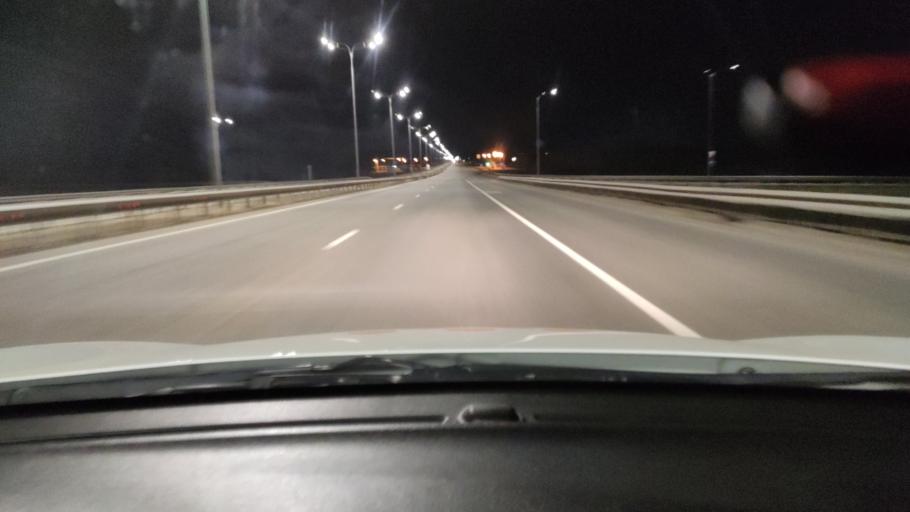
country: RU
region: Tatarstan
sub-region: Alekseyevskiy Rayon
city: Alekseyevskoye
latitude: 55.3015
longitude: 50.0569
